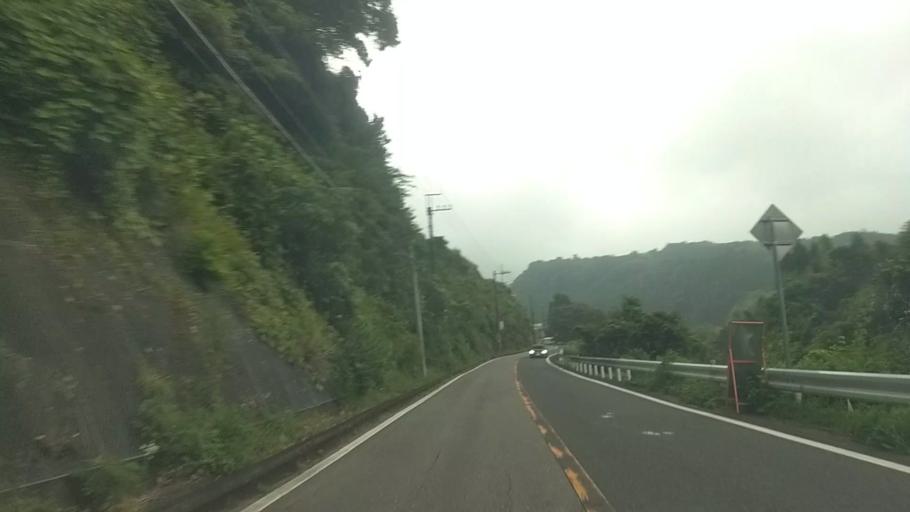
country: JP
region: Chiba
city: Katsuura
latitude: 35.2437
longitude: 140.2377
